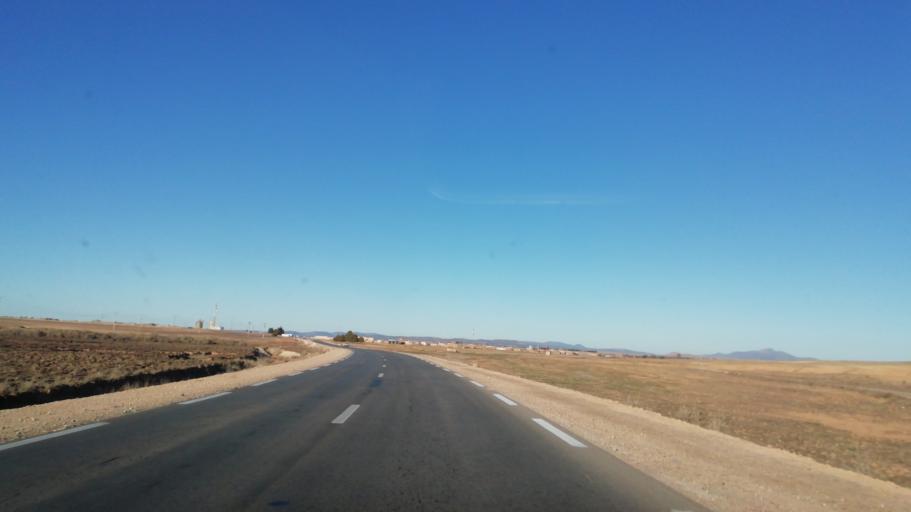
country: DZ
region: Tlemcen
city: Sebdou
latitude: 34.4704
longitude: -1.2723
